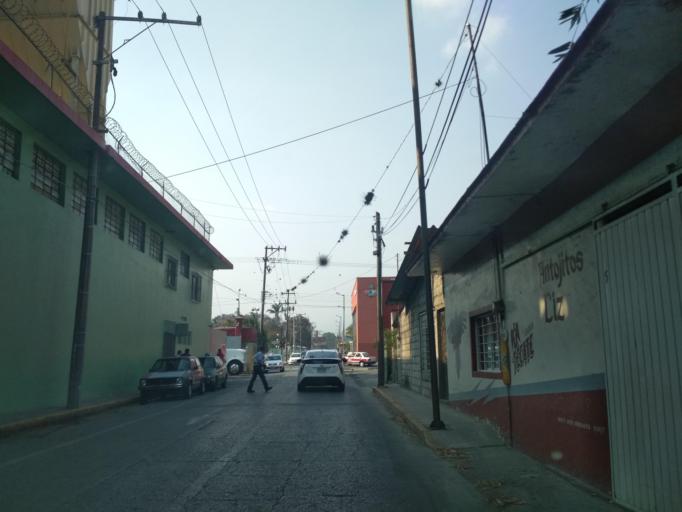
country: MX
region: Veracruz
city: Orizaba
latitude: 18.8462
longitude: -97.0872
